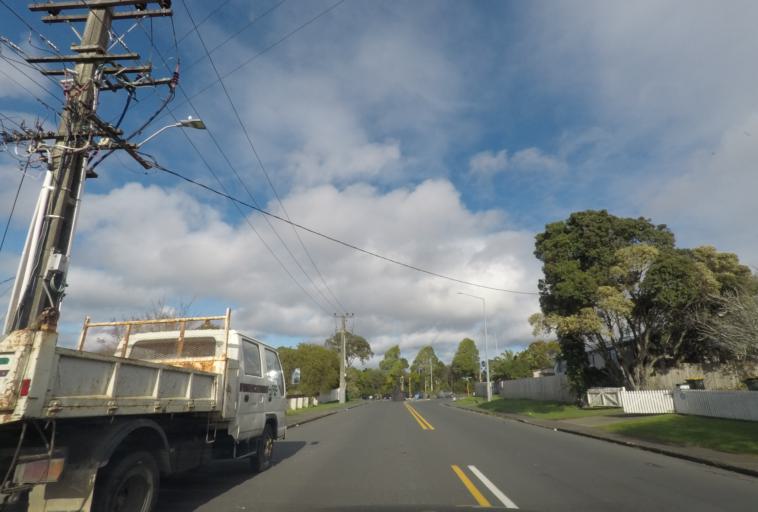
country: NZ
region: Auckland
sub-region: Auckland
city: Waitakere
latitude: -36.8975
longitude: 174.6502
